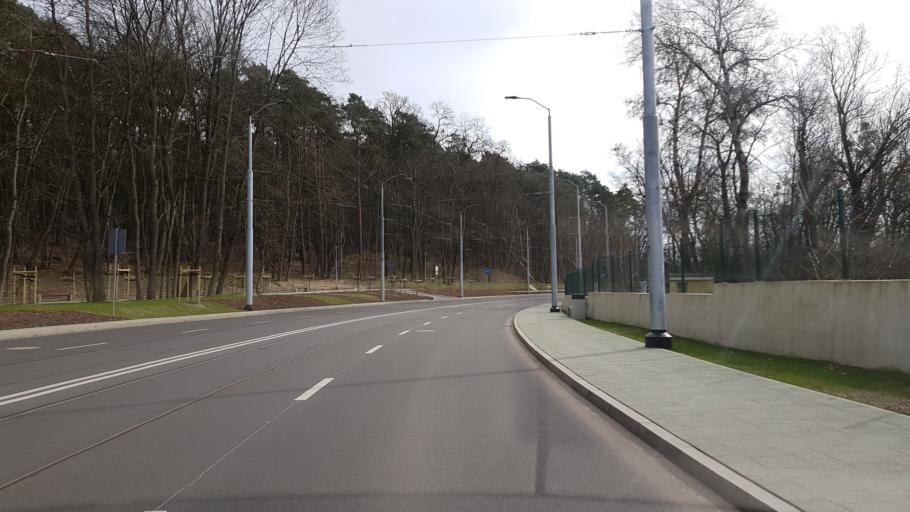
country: PL
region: West Pomeranian Voivodeship
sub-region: Szczecin
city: Szczecin
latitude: 53.4609
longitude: 14.5129
